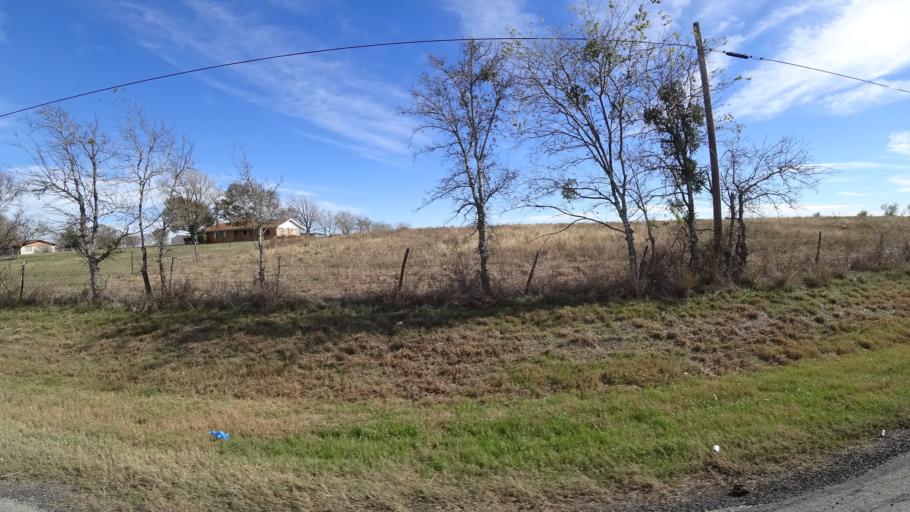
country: US
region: Texas
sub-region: Travis County
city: Onion Creek
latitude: 30.1284
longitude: -97.7105
